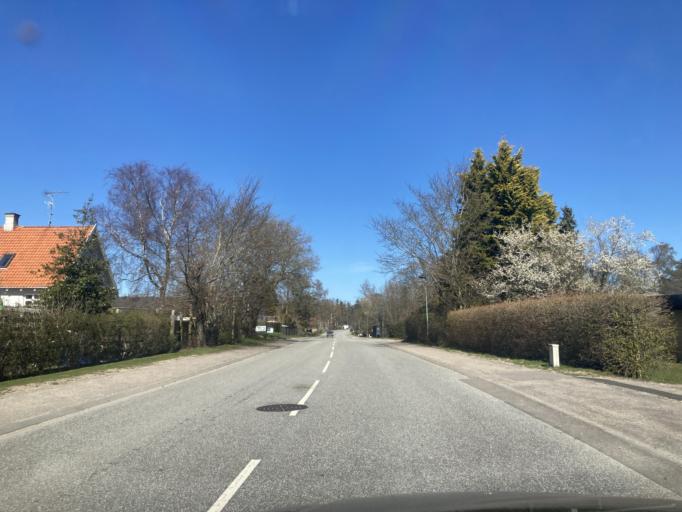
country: DK
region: Capital Region
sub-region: Gribskov Kommune
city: Graested
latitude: 56.1124
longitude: 12.2377
